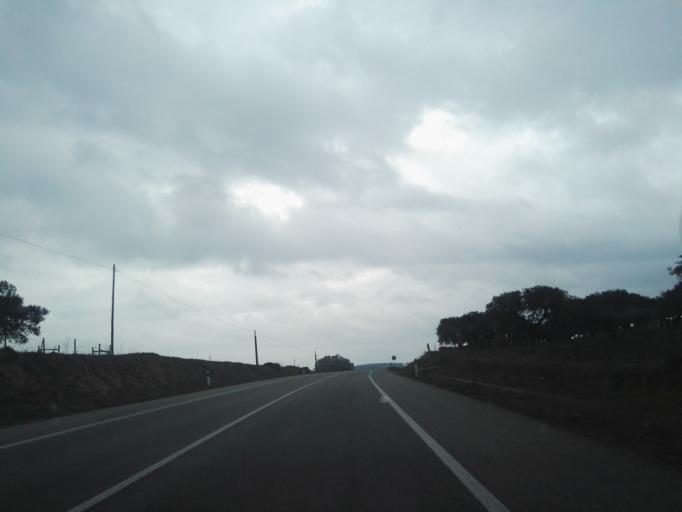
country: PT
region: Portalegre
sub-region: Portalegre
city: Alegrete
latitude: 39.1735
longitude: -7.3357
